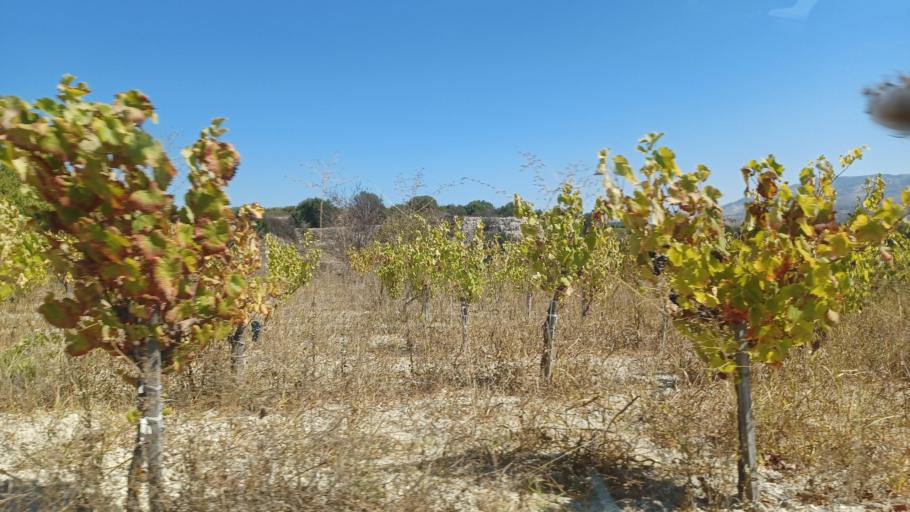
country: CY
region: Pafos
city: Mesogi
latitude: 34.8653
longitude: 32.5266
